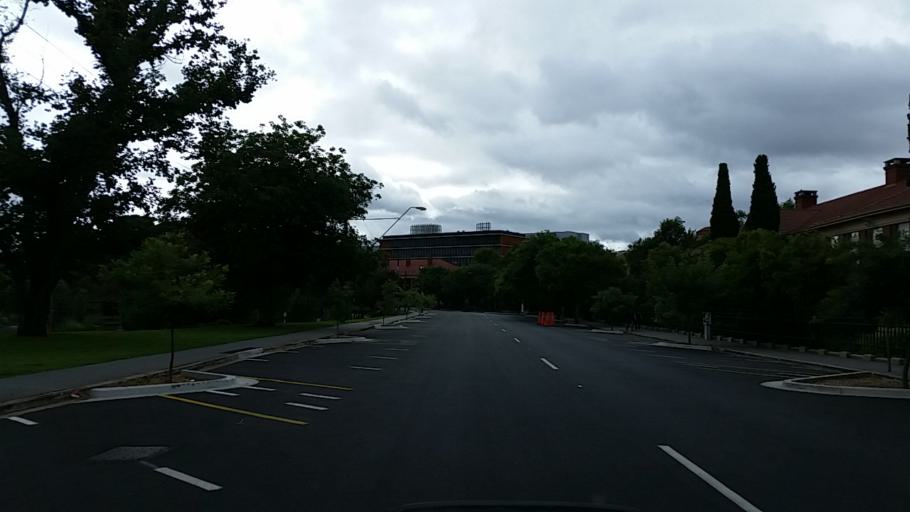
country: AU
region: South Australia
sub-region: Adelaide
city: Adelaide
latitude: -34.9173
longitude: 138.6019
